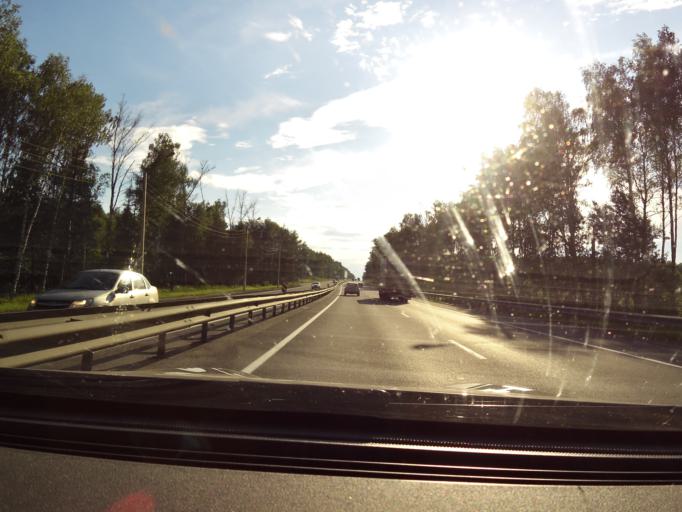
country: RU
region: Vladimir
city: Melekhovo
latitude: 56.2104
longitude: 41.2771
